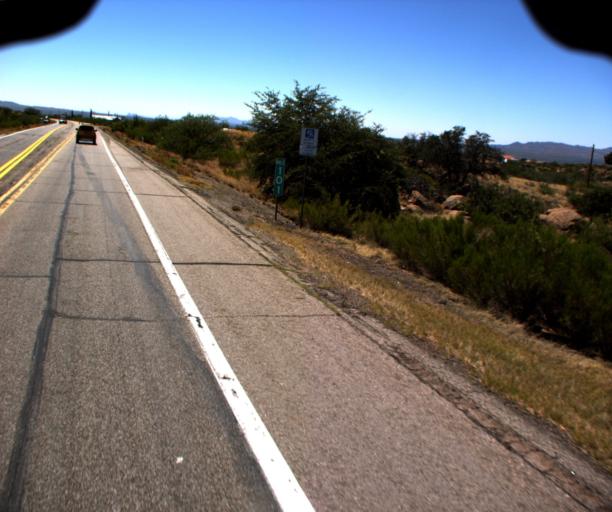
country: US
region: Arizona
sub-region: Pinal County
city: Oracle
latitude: 32.6226
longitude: -110.7893
